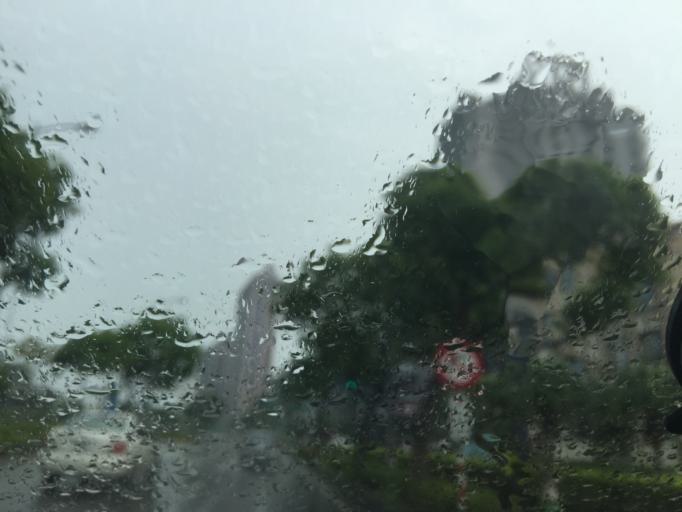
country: TW
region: Taiwan
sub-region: Hsinchu
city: Zhubei
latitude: 24.8130
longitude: 121.0346
